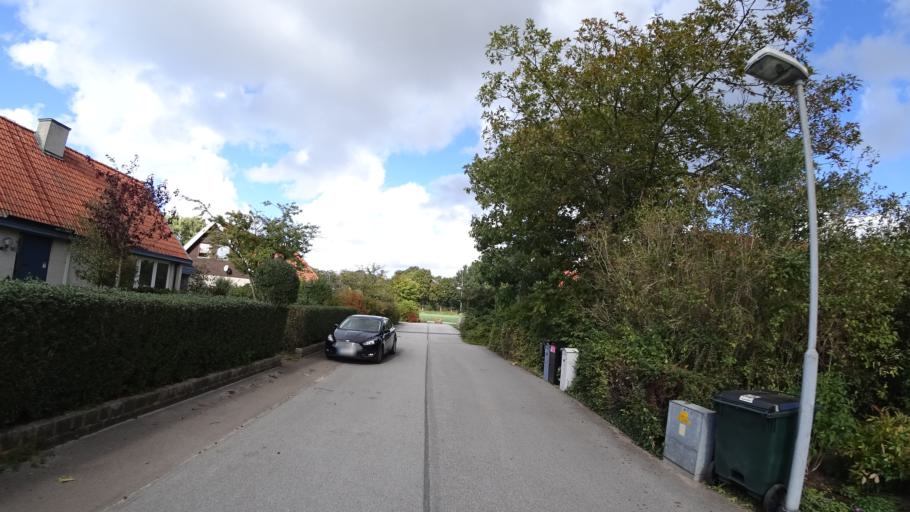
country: SE
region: Skane
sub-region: Kavlinge Kommun
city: Hofterup
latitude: 55.7729
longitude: 12.9504
